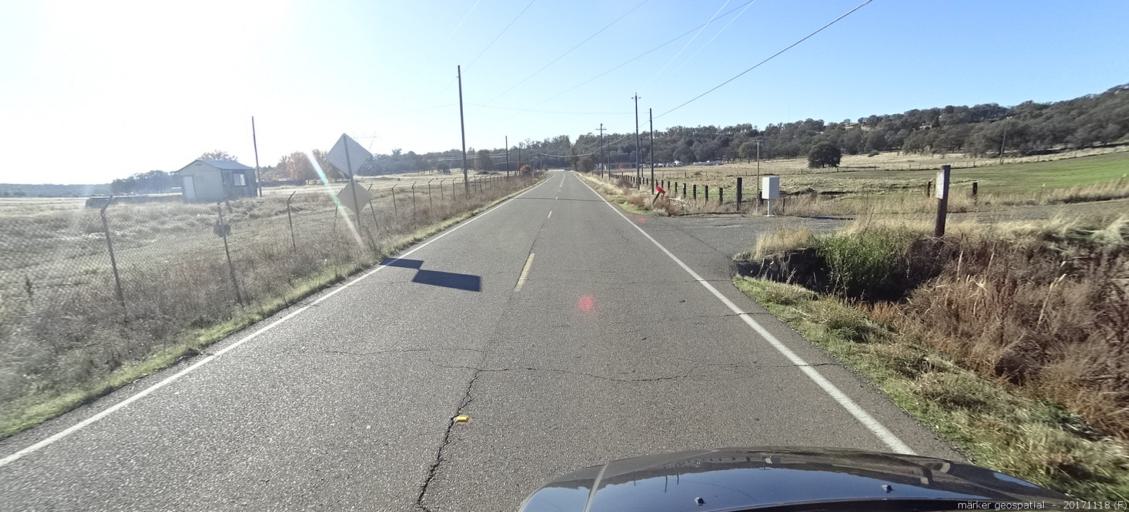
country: US
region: California
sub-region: Shasta County
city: Anderson
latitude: 40.4250
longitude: -122.2735
